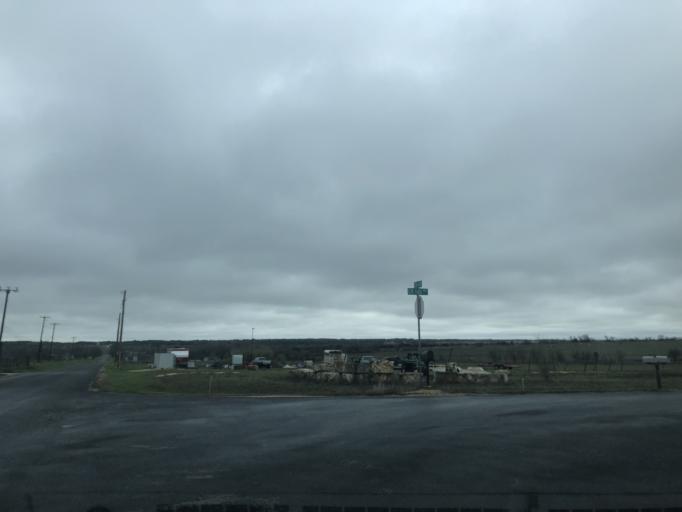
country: US
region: Texas
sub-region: Williamson County
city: Serenada
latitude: 30.7598
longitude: -97.6056
